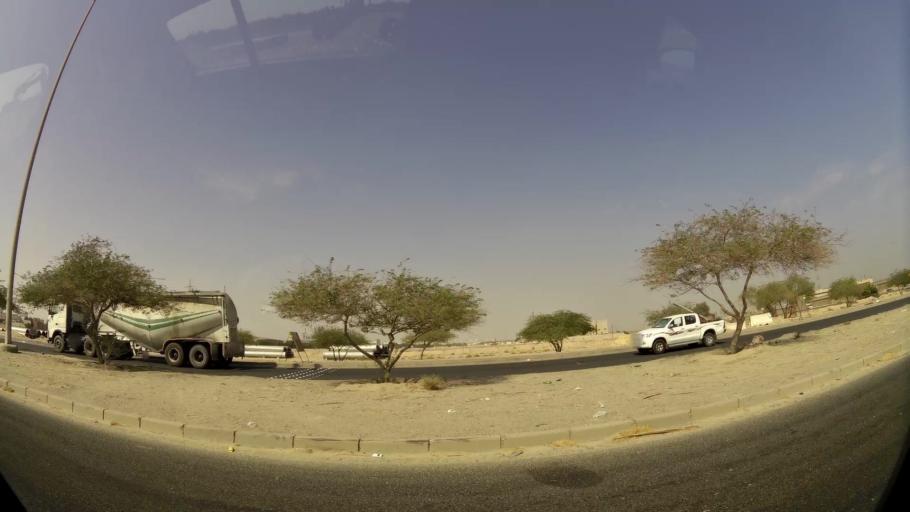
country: KW
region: Al Ahmadi
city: Al Fahahil
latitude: 28.9951
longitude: 48.1417
